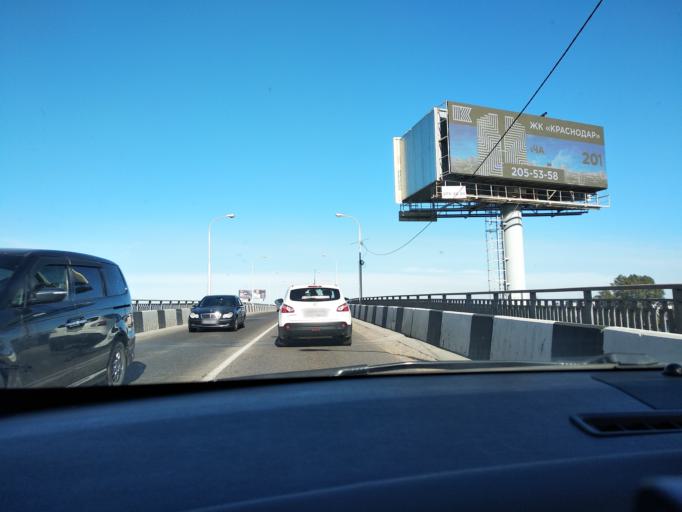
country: RU
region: Adygeya
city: Yablonovskiy
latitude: 44.9945
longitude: 38.9563
